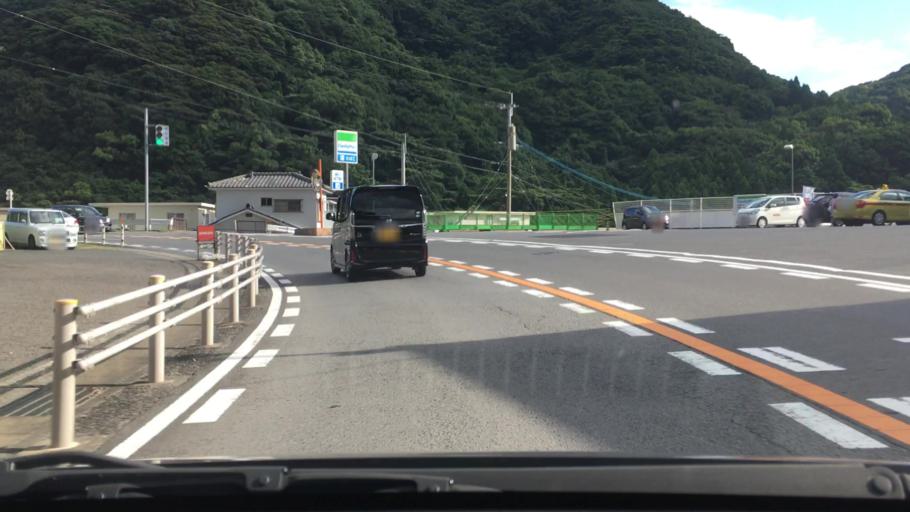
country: JP
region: Nagasaki
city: Togitsu
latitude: 32.8103
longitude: 129.8105
